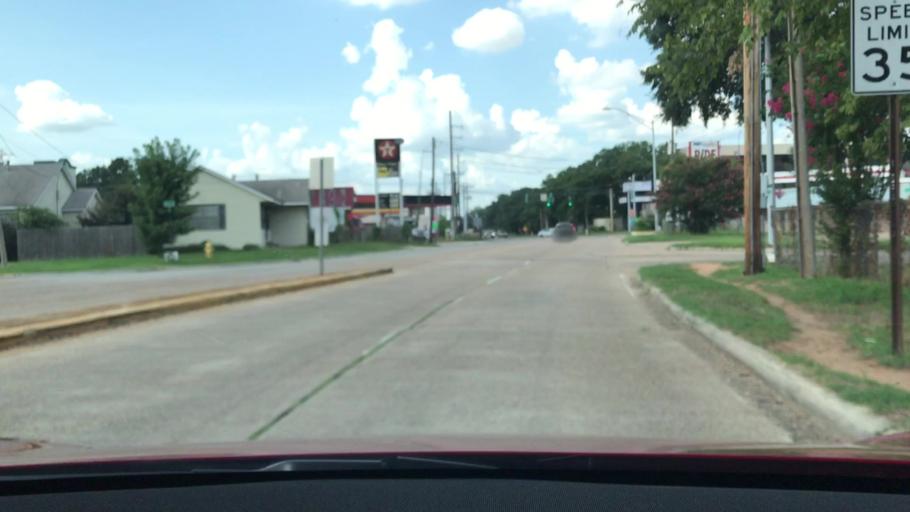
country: US
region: Louisiana
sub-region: Bossier Parish
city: Bossier City
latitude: 32.5146
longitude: -93.7264
